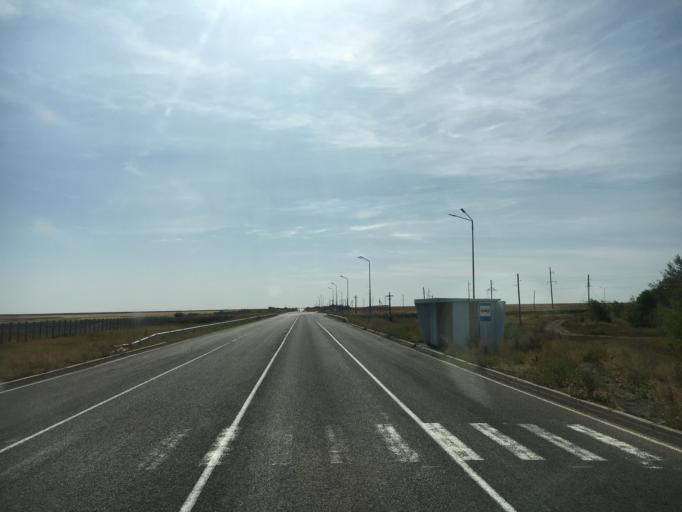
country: KZ
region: Batys Qazaqstan
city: Peremetnoe
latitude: 51.1352
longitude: 50.9073
